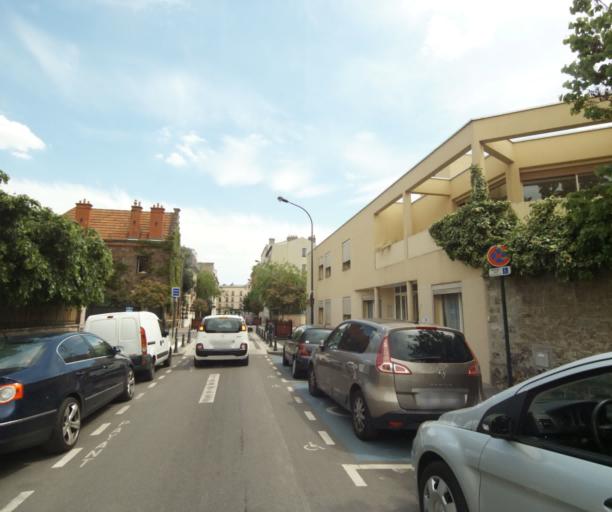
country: FR
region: Ile-de-France
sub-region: Departement des Hauts-de-Seine
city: Asnieres-sur-Seine
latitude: 48.9130
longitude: 2.2934
